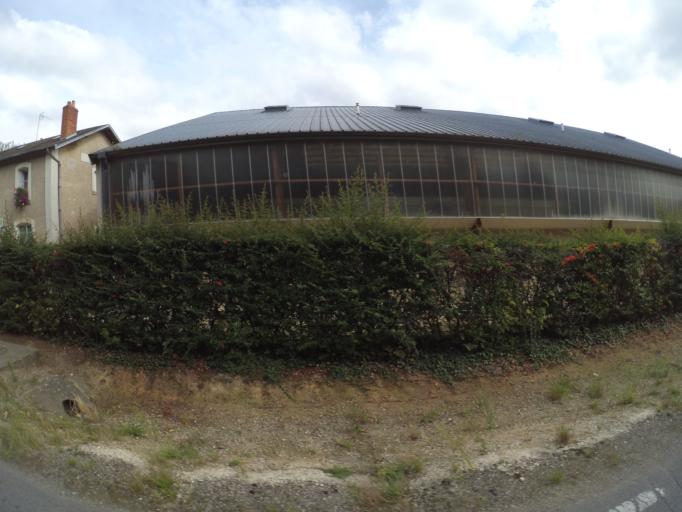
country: FR
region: Centre
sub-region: Departement d'Indre-et-Loire
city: Vernou-sur-Brenne
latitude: 47.4207
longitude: 0.8423
